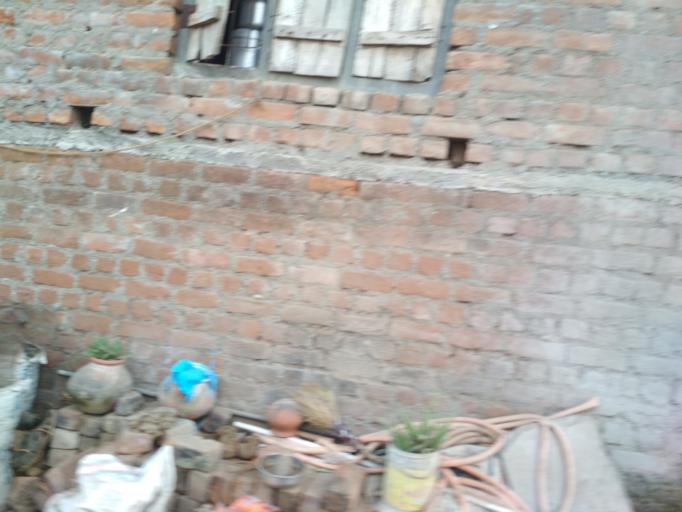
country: IN
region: Maharashtra
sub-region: Nagpur Division
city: Mohpa
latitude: 21.3091
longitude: 78.8286
